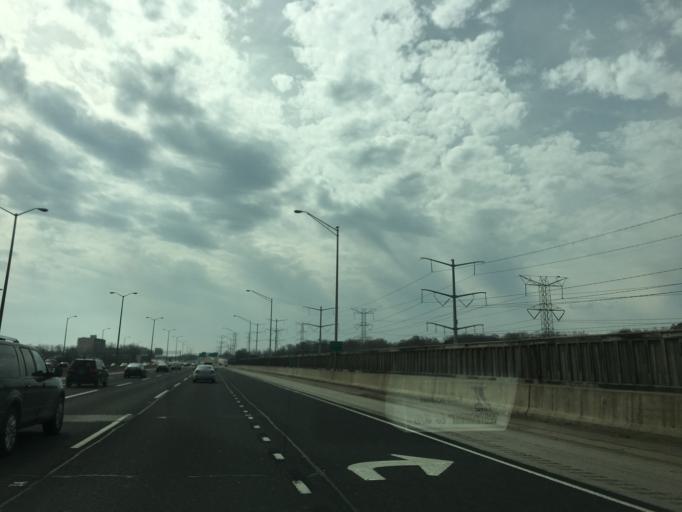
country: US
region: Illinois
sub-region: DuPage County
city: Lisle
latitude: 41.7963
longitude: -88.0571
